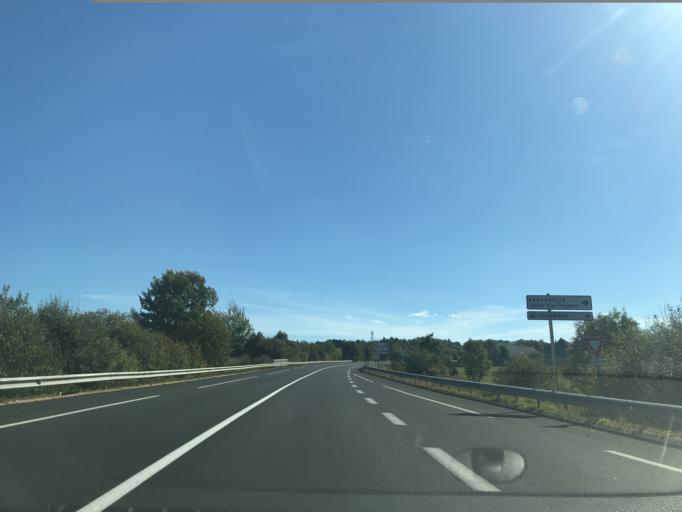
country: FR
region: Auvergne
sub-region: Departement du Puy-de-Dome
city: Saint-Sauves-d'Auvergne
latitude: 45.6670
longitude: 2.7257
